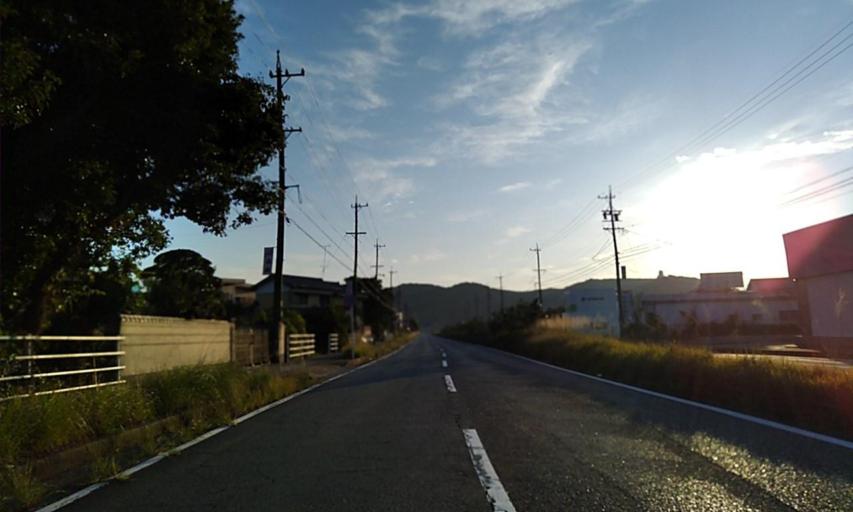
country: JP
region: Mie
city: Ise
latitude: 34.5048
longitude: 136.7670
